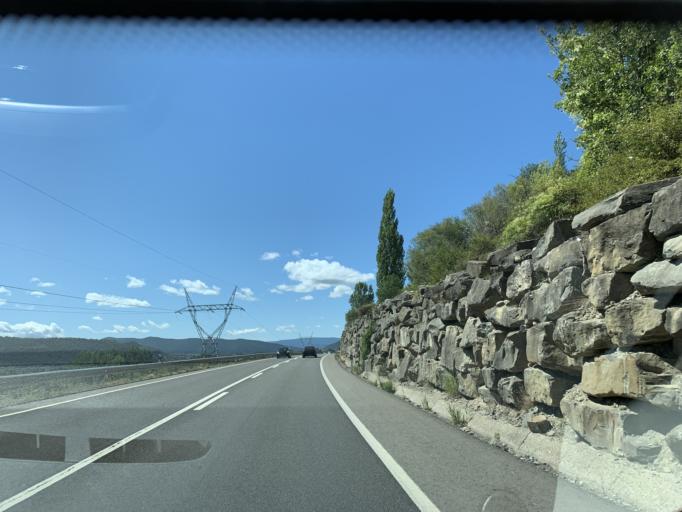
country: ES
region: Aragon
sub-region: Provincia de Huesca
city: Biescas
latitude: 42.5693
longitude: -0.3258
